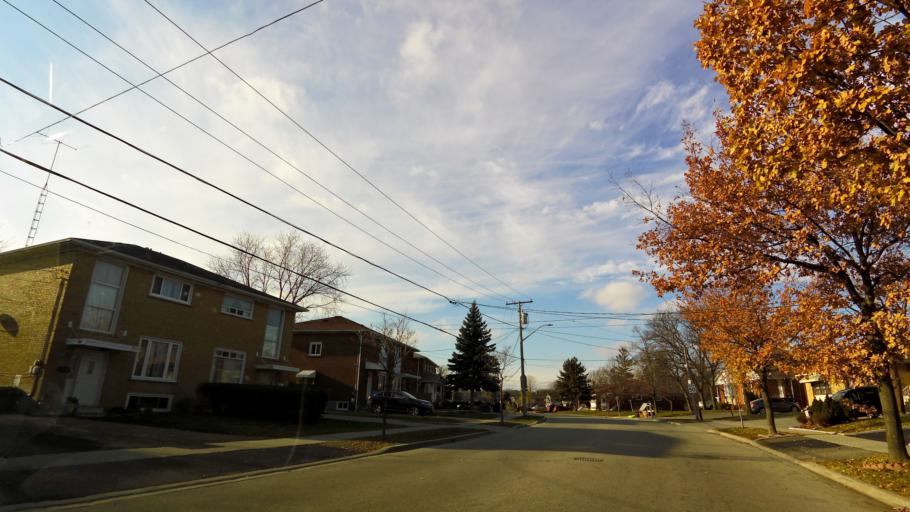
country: CA
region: Ontario
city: Mississauga
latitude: 43.5627
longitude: -79.6625
